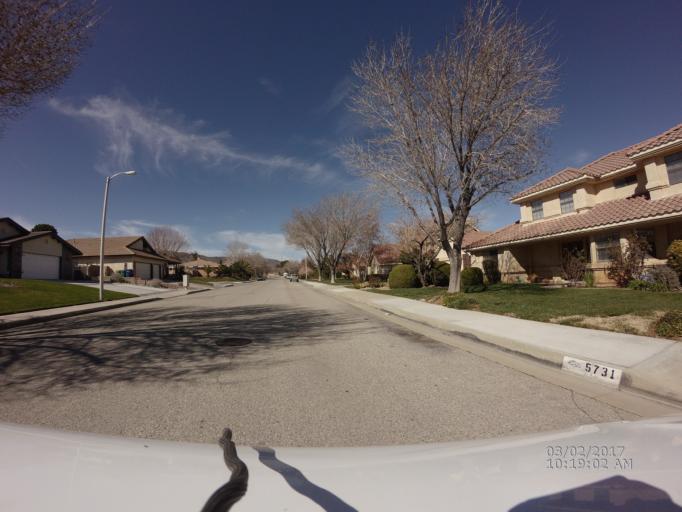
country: US
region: California
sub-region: Los Angeles County
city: Quartz Hill
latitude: 34.6400
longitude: -118.2328
